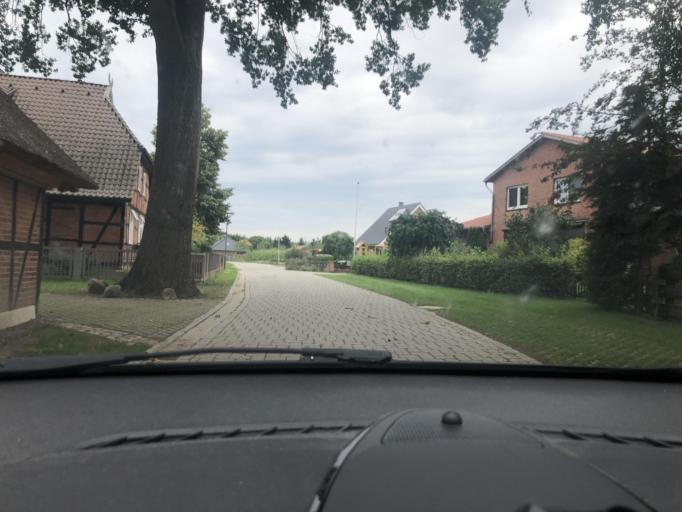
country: DE
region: Mecklenburg-Vorpommern
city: Nostorf
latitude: 53.3528
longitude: 10.6673
